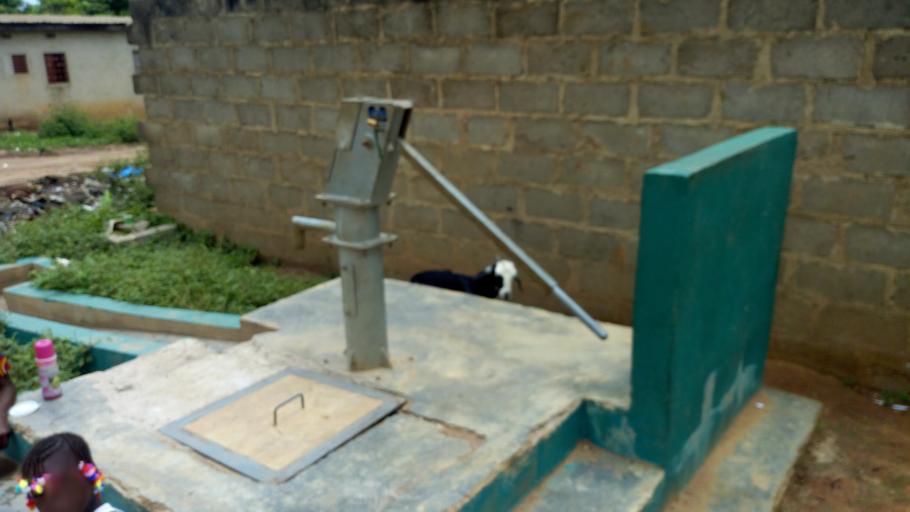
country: CI
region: Vallee du Bandama
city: Bouake
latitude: 7.7312
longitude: -5.0446
